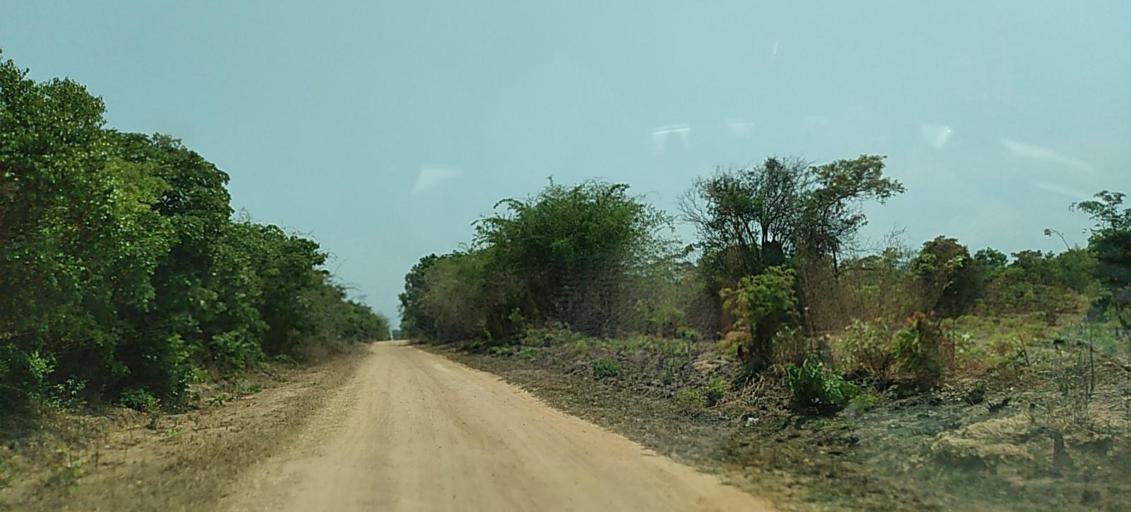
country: ZM
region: Copperbelt
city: Kalulushi
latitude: -12.9391
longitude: 28.1605
